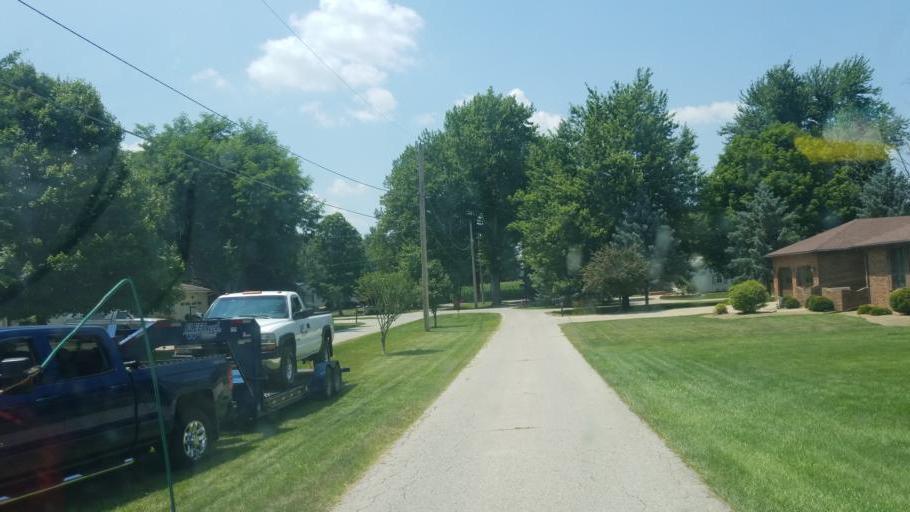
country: US
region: Ohio
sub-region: Richland County
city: Shelby
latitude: 40.8656
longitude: -82.6665
